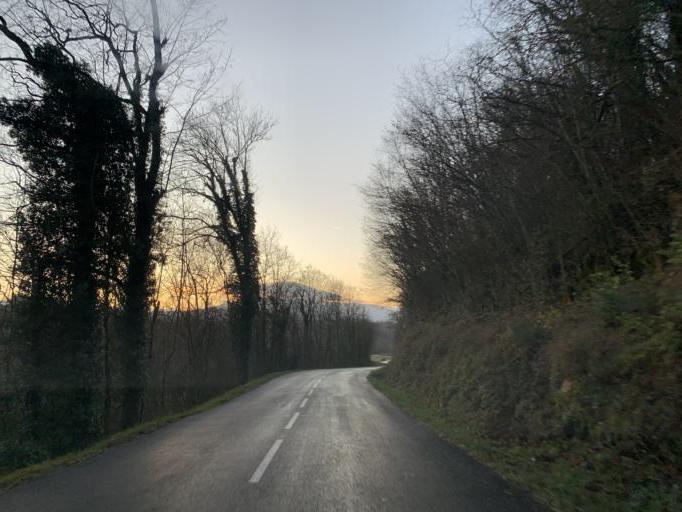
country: FR
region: Rhone-Alpes
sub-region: Departement de l'Ain
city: Belley
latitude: 45.7847
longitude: 5.6538
